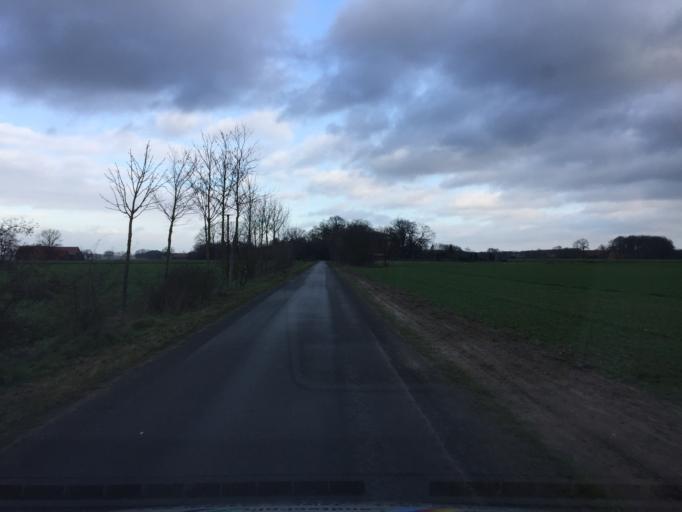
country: DE
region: Lower Saxony
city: Steyerberg
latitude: 52.5140
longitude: 8.9980
